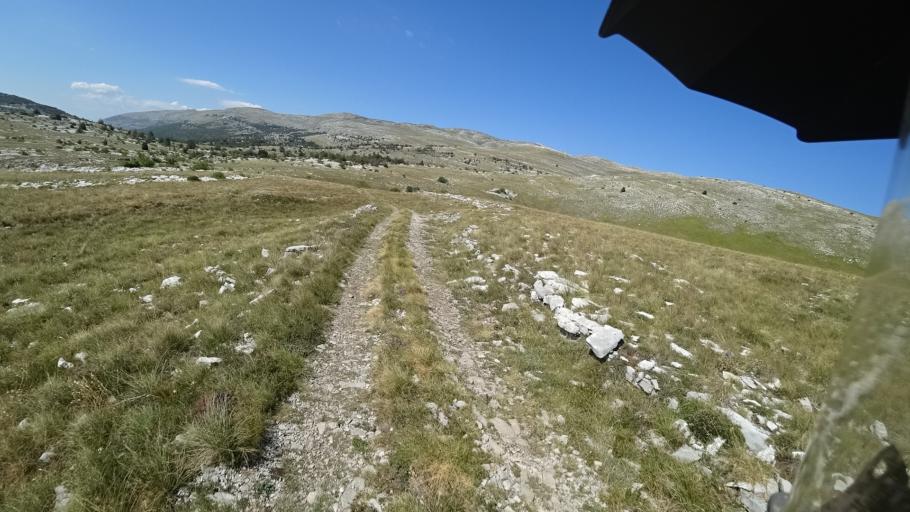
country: HR
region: Splitsko-Dalmatinska
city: Hrvace
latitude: 43.9015
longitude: 16.5958
